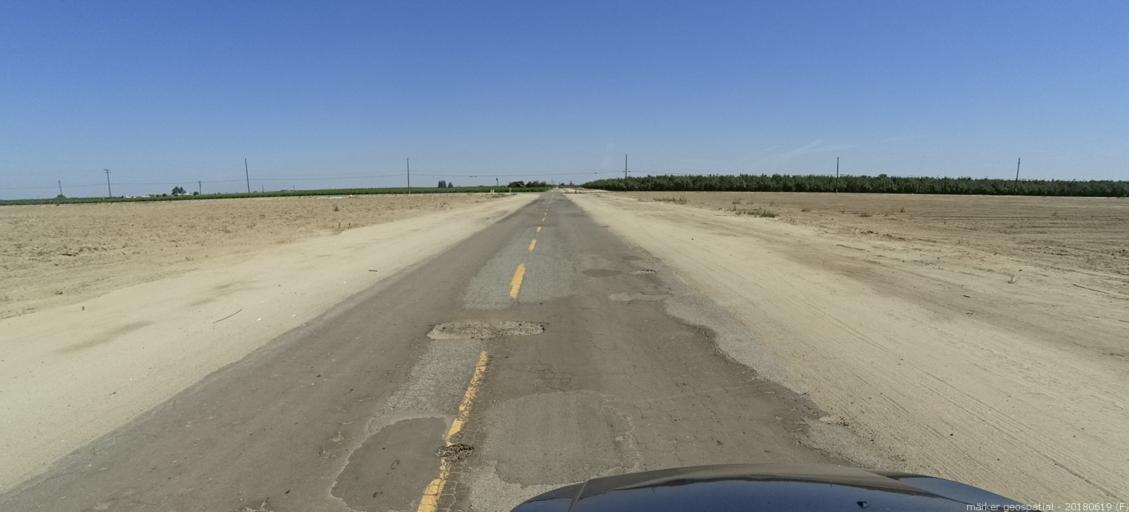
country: US
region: California
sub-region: Fresno County
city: Biola
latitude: 36.8496
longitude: -120.0650
